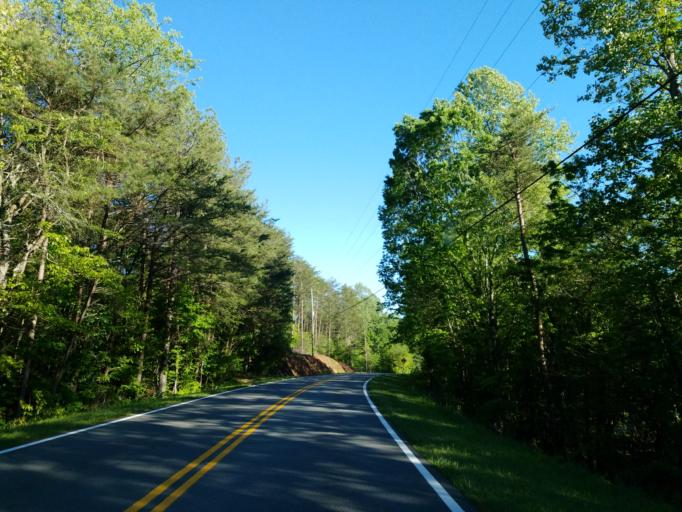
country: US
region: Georgia
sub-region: Gilmer County
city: Ellijay
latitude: 34.6739
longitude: -84.3684
